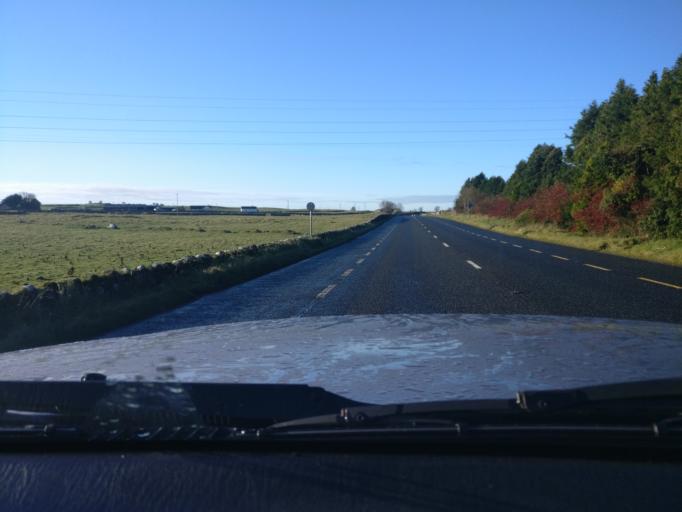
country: IE
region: Connaught
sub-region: County Galway
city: Loughrea
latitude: 53.2073
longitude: -8.5222
